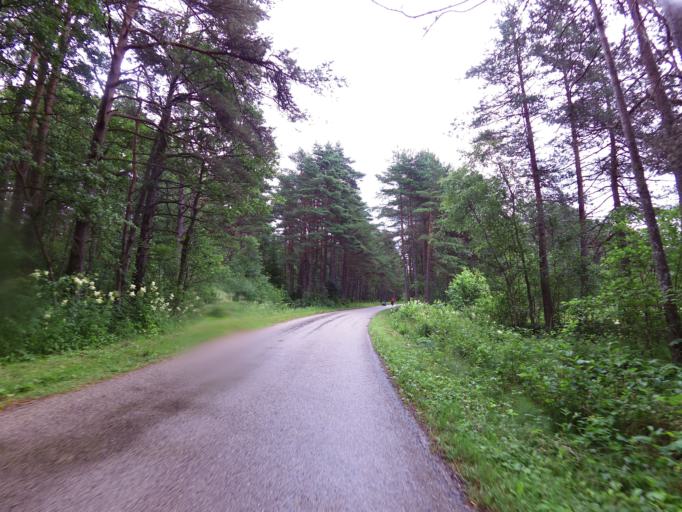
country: EE
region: Laeaene
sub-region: Vormsi vald
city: Hullo
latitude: 59.0045
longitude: 23.2640
